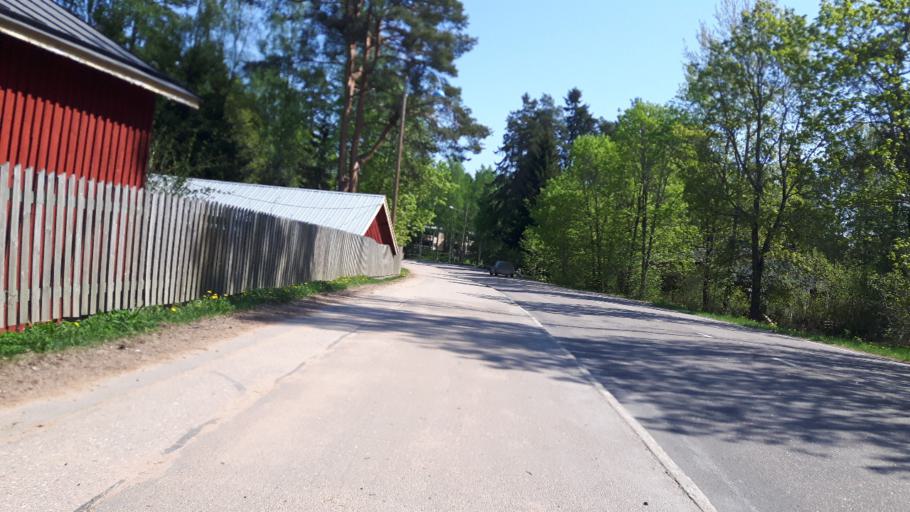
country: FI
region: Kymenlaakso
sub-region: Kotka-Hamina
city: Pyhtaeae
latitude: 60.4911
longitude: 26.5483
